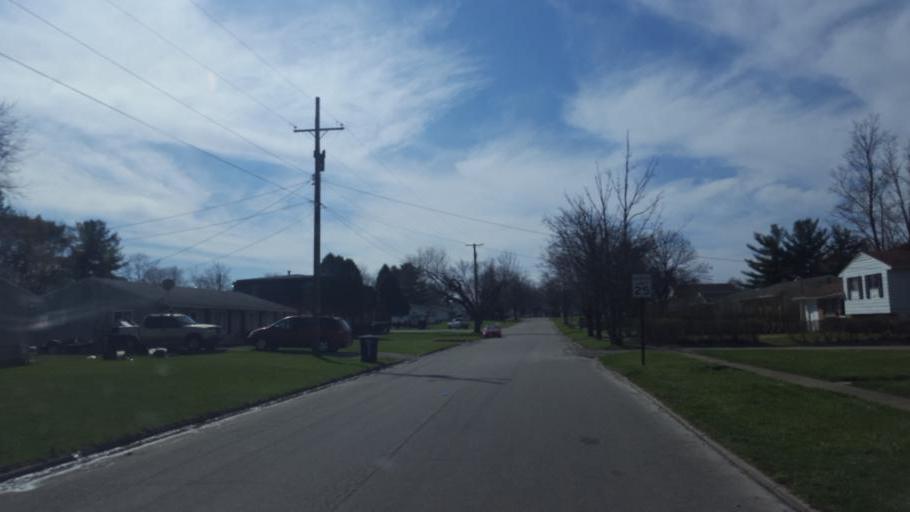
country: US
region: Ohio
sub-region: Richland County
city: Mansfield
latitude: 40.7729
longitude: -82.5422
